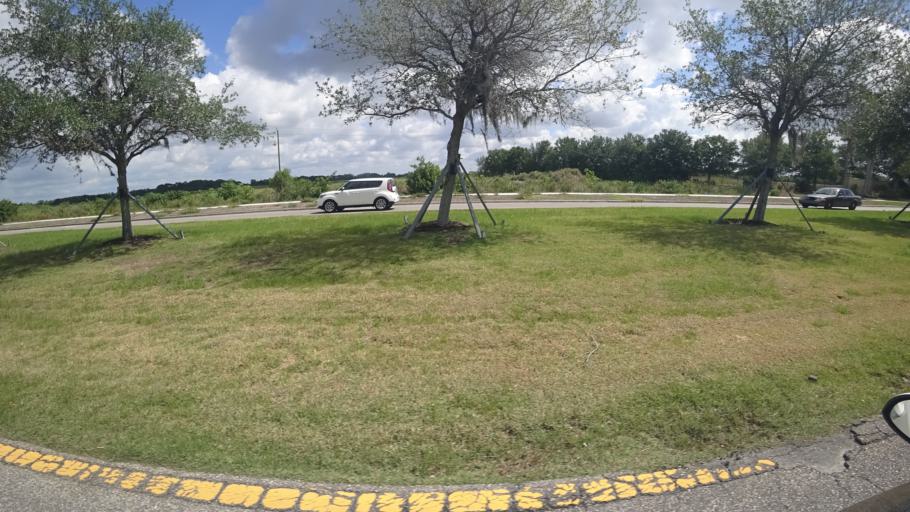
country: US
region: Florida
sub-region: Manatee County
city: Bayshore Gardens
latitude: 27.4327
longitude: -82.6192
